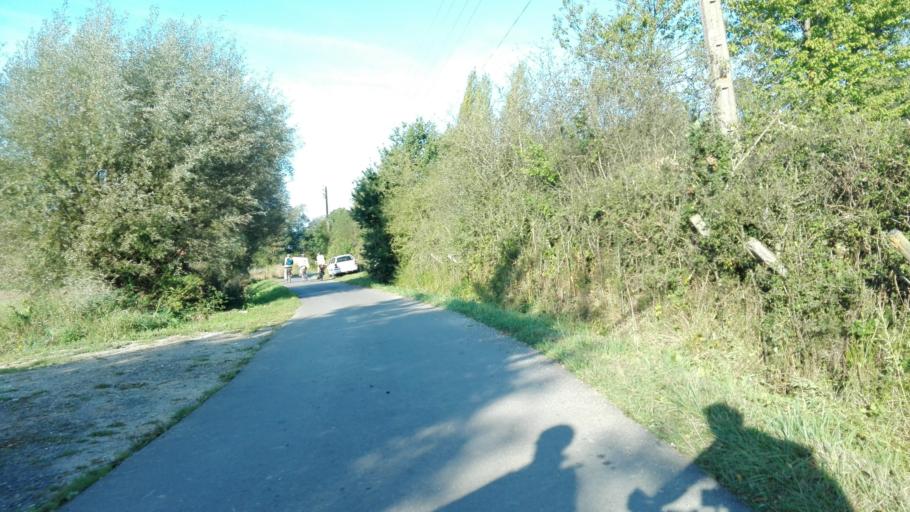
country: FR
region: Nord-Pas-de-Calais
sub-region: Departement du Pas-de-Calais
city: Eperlecques
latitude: 50.8251
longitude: 2.1752
